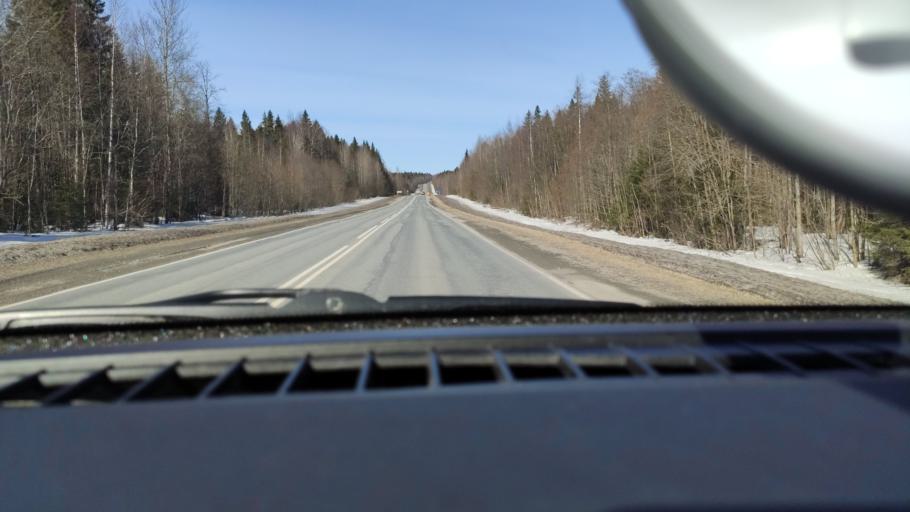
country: RU
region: Perm
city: Perm
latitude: 58.1570
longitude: 56.2495
